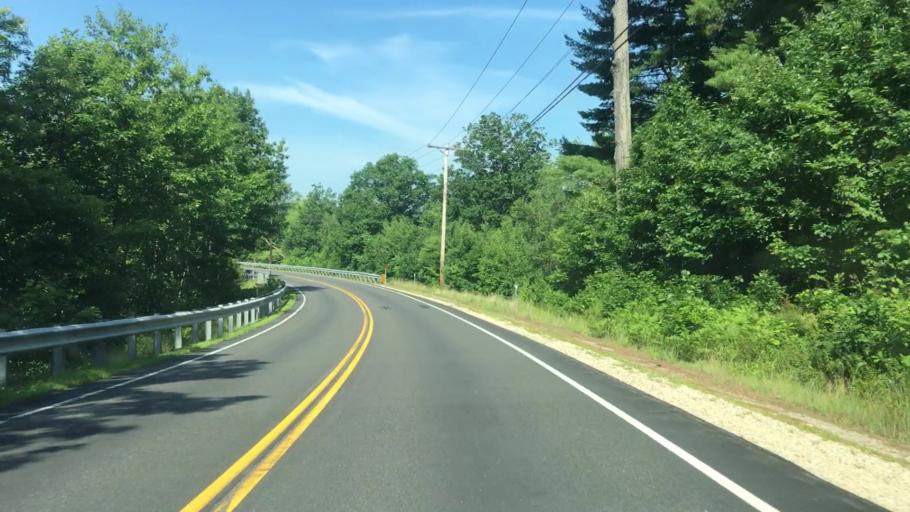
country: US
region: New Hampshire
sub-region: Merrimack County
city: Contoocook
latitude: 43.1939
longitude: -71.7356
